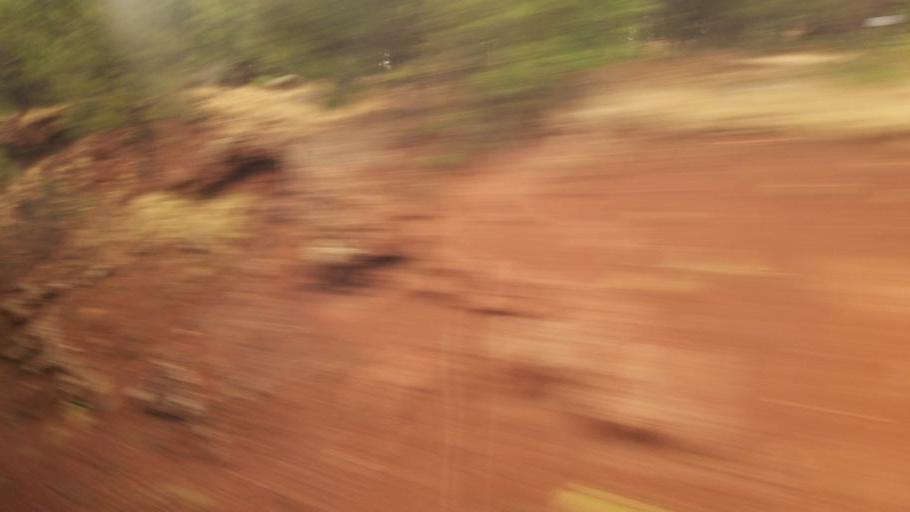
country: US
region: Arizona
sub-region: Coconino County
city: Parks
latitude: 35.2509
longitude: -111.9023
